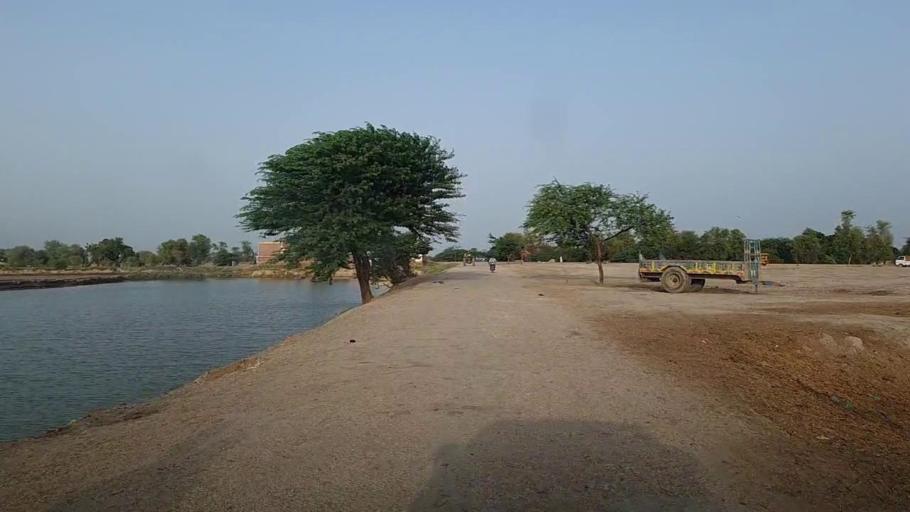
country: PK
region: Sindh
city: Mehar
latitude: 27.1633
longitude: 67.7912
